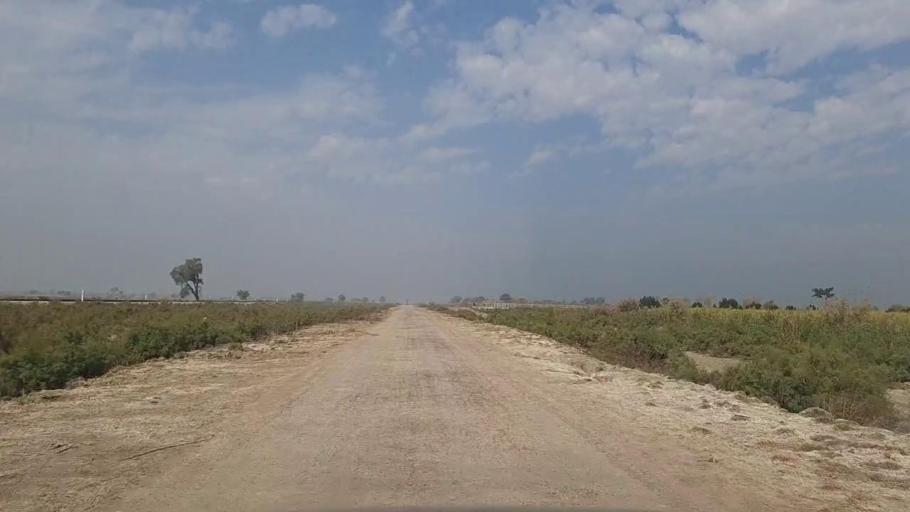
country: PK
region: Sindh
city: Daur
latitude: 26.3899
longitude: 68.3506
